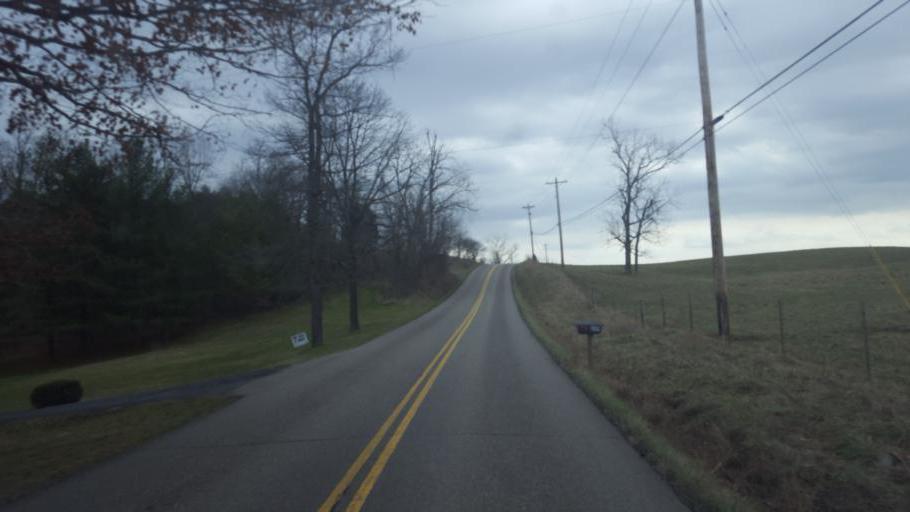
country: US
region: Ohio
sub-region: Gallia County
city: Gallipolis
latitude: 38.7663
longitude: -82.3751
